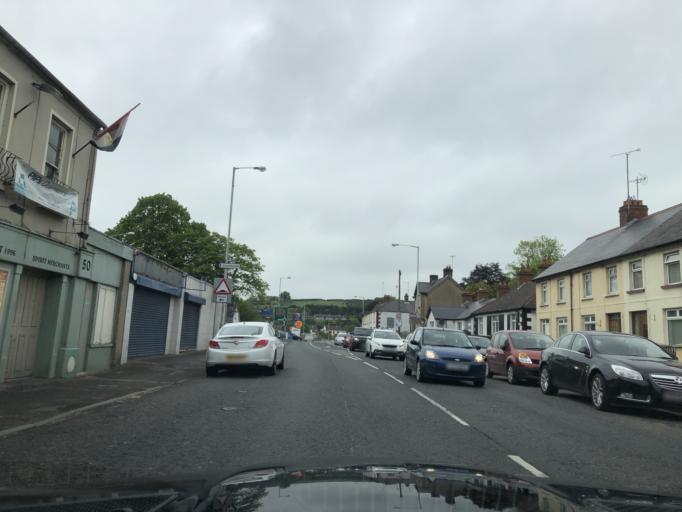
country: GB
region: Northern Ireland
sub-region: Down District
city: Downpatrick
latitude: 54.3326
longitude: -5.7160
